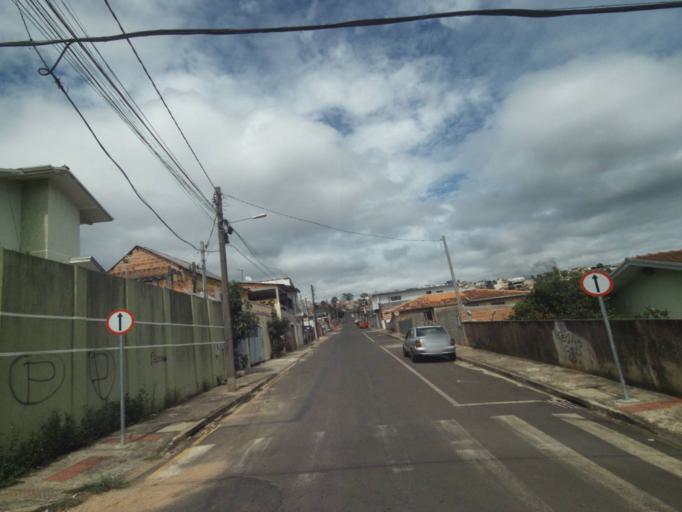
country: BR
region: Parana
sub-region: Telemaco Borba
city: Telemaco Borba
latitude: -24.3324
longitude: -50.6380
